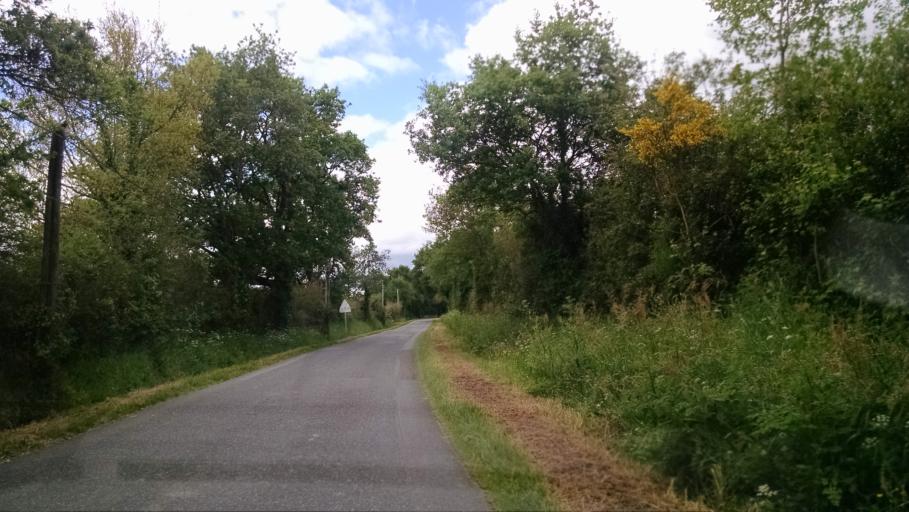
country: FR
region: Pays de la Loire
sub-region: Departement de la Loire-Atlantique
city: Remouille
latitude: 47.0333
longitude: -1.3843
